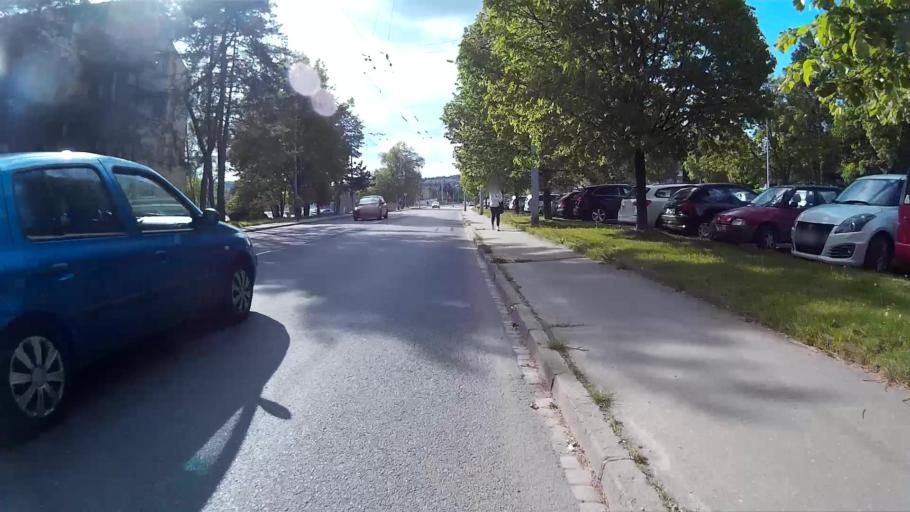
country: CZ
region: South Moravian
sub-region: Mesto Brno
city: Brno
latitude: 49.2151
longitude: 16.5834
